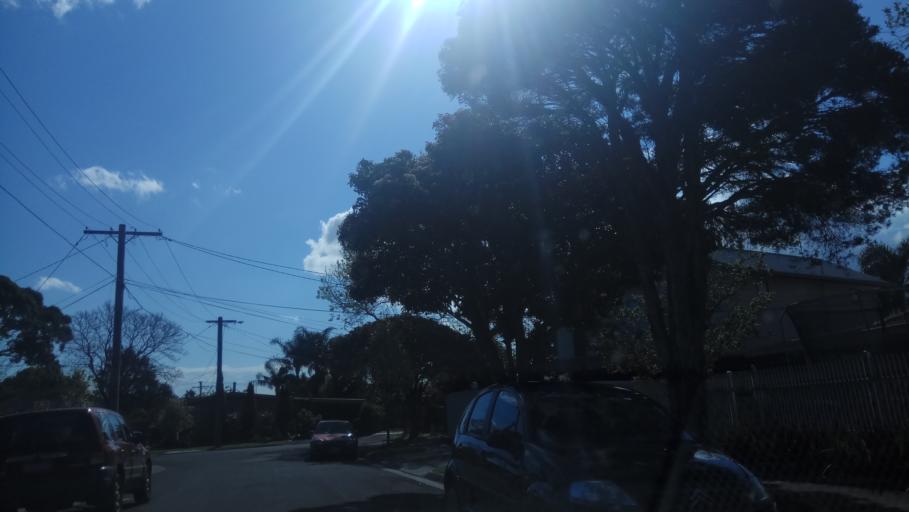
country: AU
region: Victoria
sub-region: Kingston
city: Dingley Village
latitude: -37.9841
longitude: 145.1281
